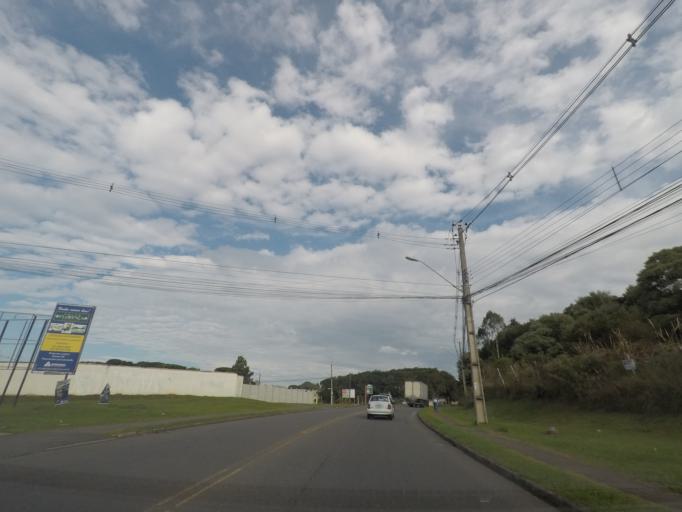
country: BR
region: Parana
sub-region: Sao Jose Dos Pinhais
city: Sao Jose dos Pinhais
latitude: -25.5575
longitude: -49.2919
